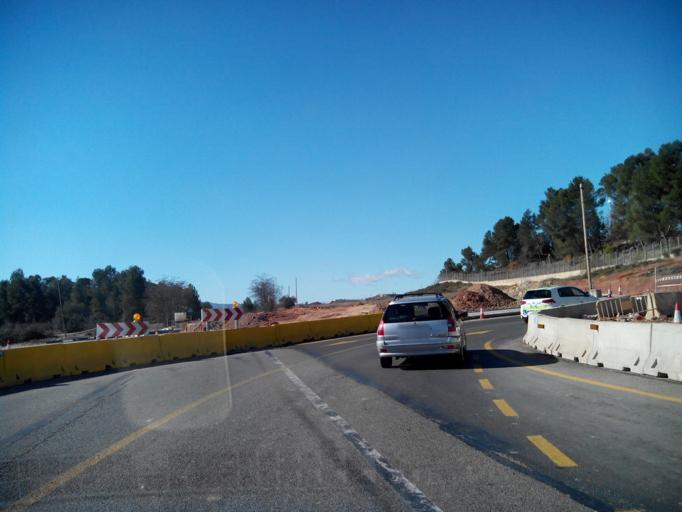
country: ES
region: Catalonia
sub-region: Provincia de Barcelona
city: Sant Fruitos de Bages
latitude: 41.7572
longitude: 1.8681
